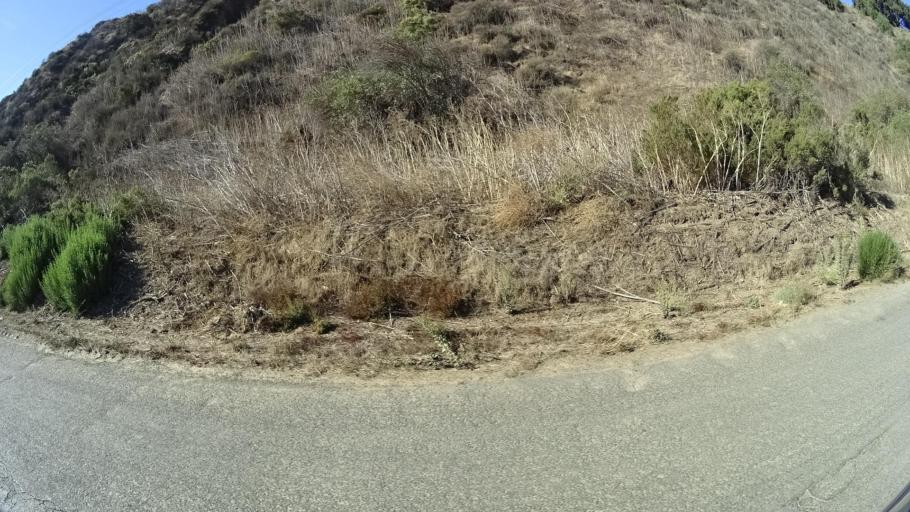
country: US
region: California
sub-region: Monterey County
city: Soledad
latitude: 36.3975
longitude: -121.3712
